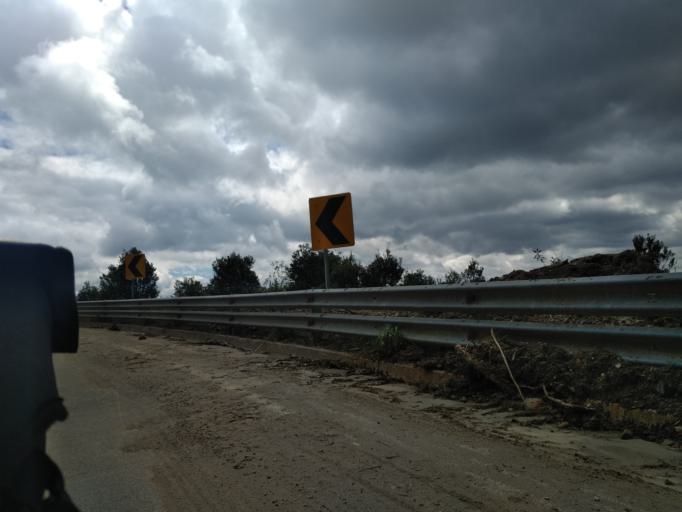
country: EC
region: Zamora-Chinchipe
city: Zamora
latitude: -4.4380
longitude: -79.1470
